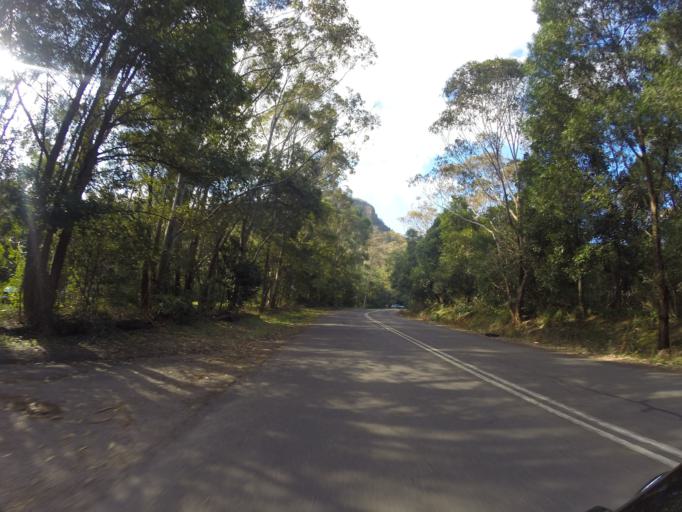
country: AU
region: New South Wales
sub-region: Wollongong
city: Mount Keira
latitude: -34.4077
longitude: 150.8497
